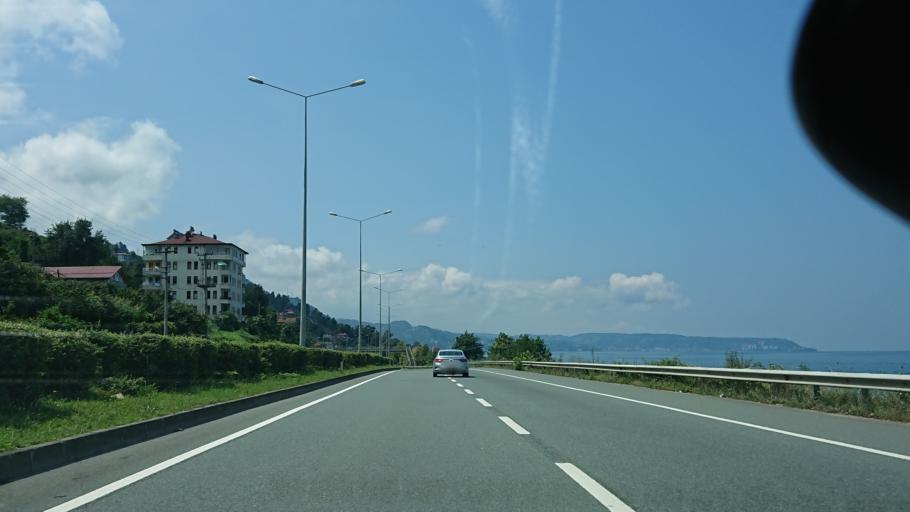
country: TR
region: Trabzon
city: Surmene
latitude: 40.9141
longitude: 40.1804
